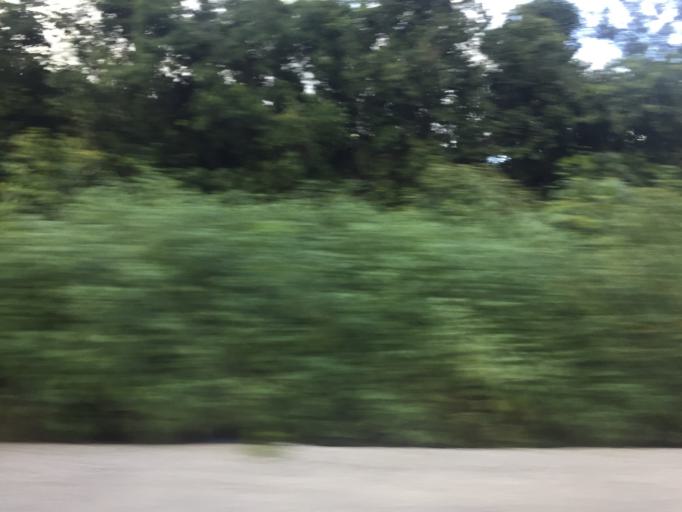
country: MX
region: Quintana Roo
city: Tulum
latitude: 20.2917
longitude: -87.5091
